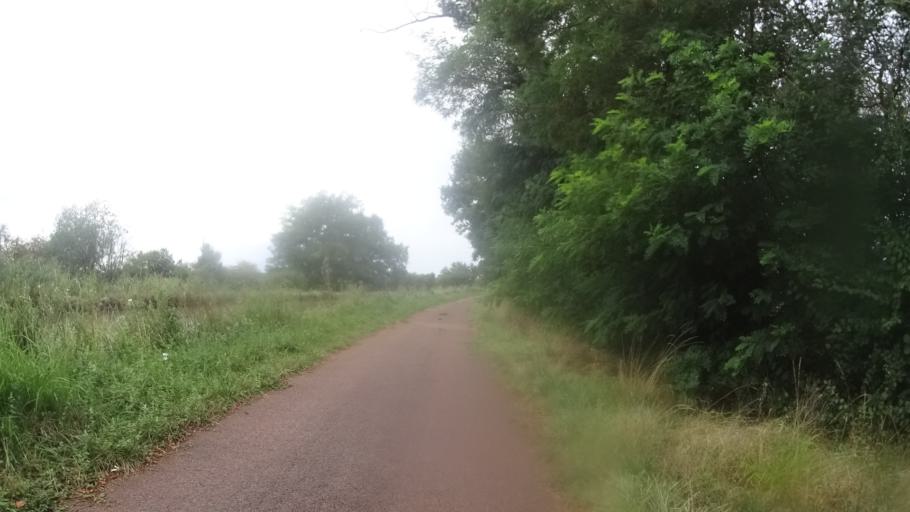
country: FR
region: Bourgogne
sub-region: Departement de la Nievre
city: Imphy
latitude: 46.8680
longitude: 3.2771
